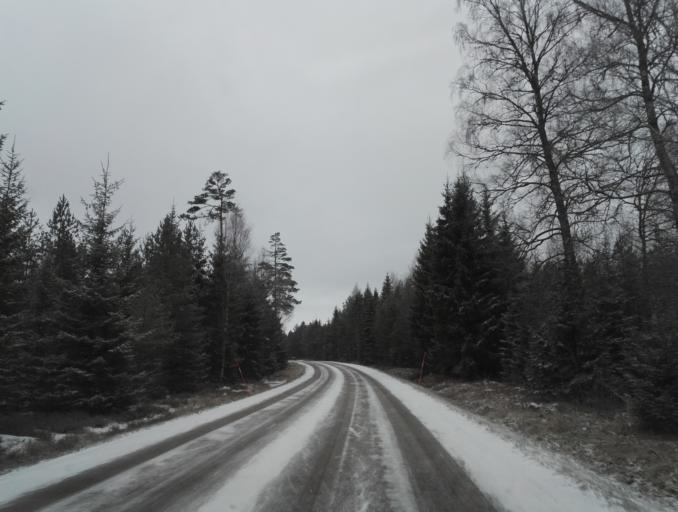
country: SE
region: Kronoberg
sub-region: Lessebo Kommun
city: Lessebo
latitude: 56.8193
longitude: 15.3786
